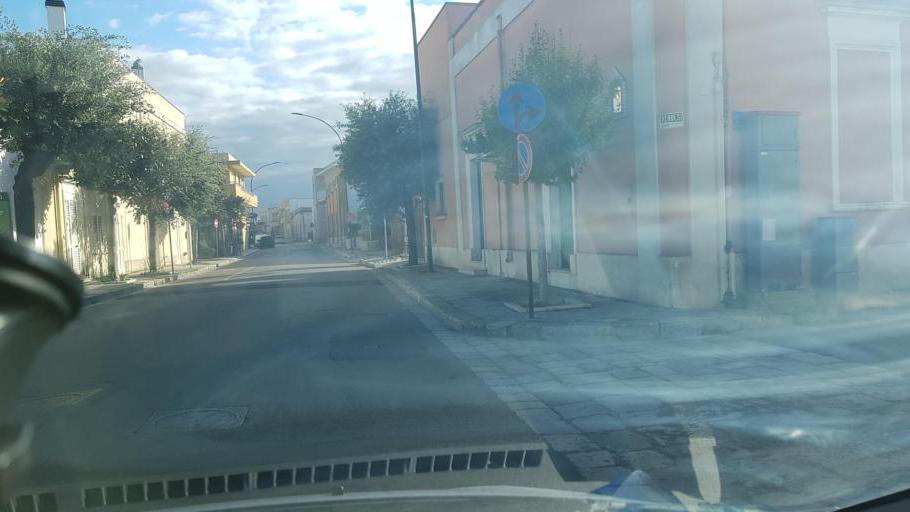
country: IT
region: Apulia
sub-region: Provincia di Lecce
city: Guagnano
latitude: 40.4001
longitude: 17.9527
